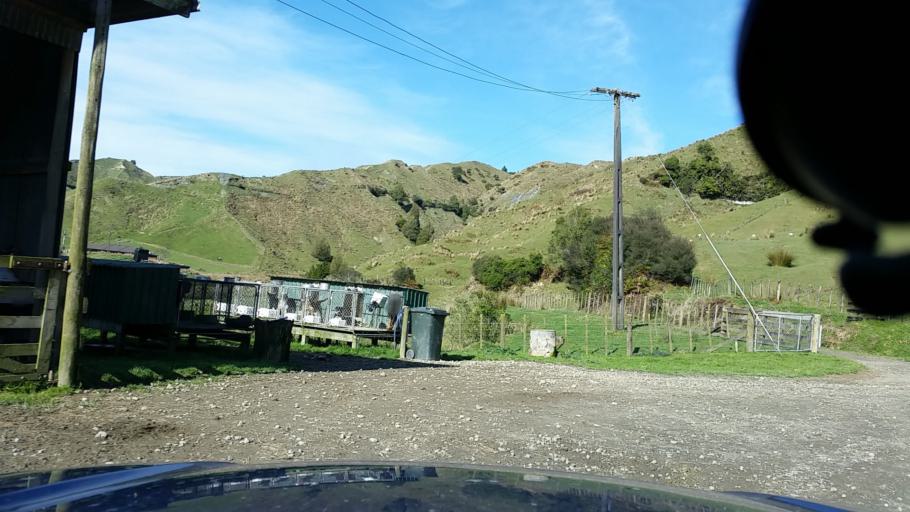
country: NZ
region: Taranaki
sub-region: New Plymouth District
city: Waitara
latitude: -39.0511
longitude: 174.7473
